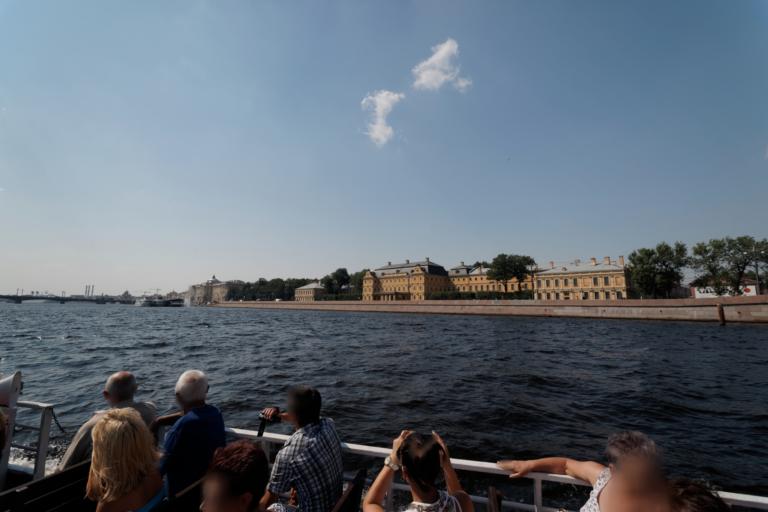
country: RU
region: St.-Petersburg
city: Saint Petersburg
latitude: 59.9385
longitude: 30.2988
